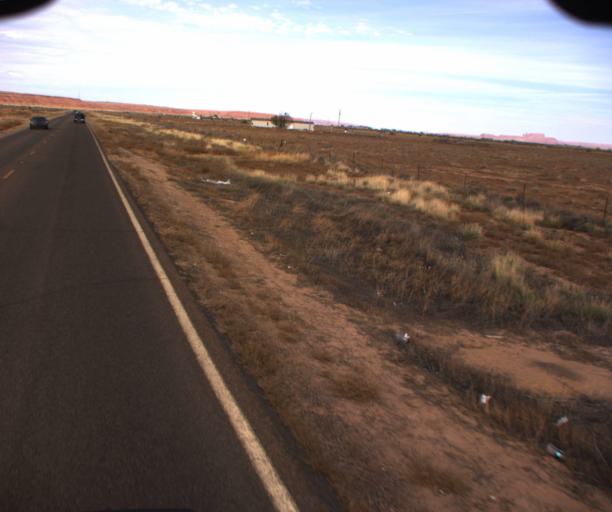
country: US
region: Arizona
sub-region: Apache County
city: Many Farms
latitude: 36.3242
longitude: -109.6183
